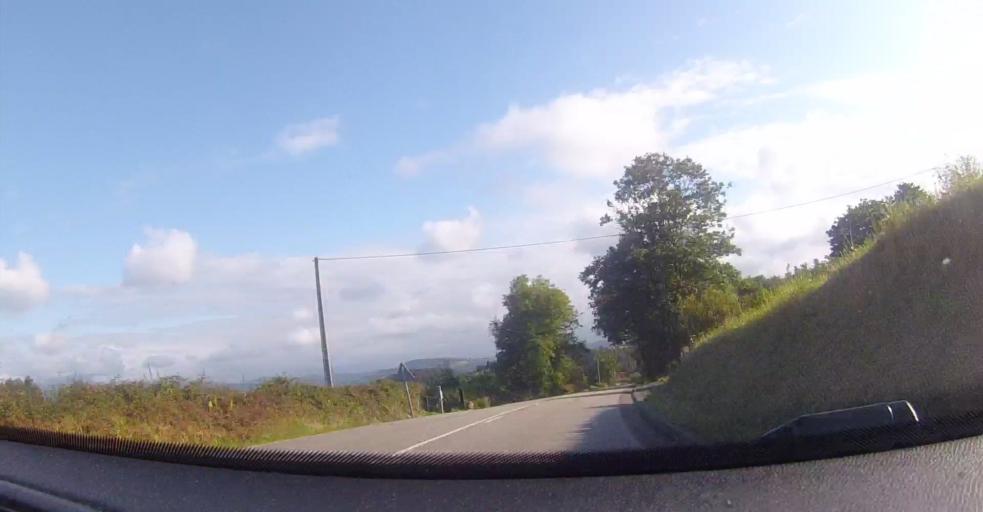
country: ES
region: Asturias
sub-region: Province of Asturias
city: Villaviciosa
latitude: 43.5391
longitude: -5.3950
